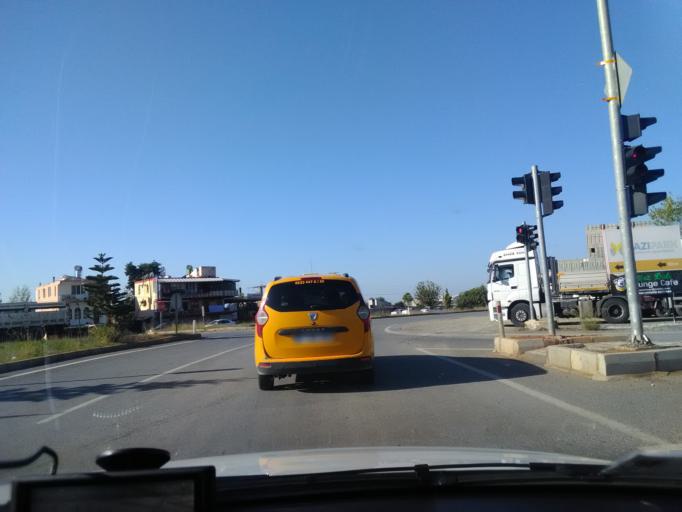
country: TR
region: Antalya
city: Gazipasa
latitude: 36.2949
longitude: 32.2871
